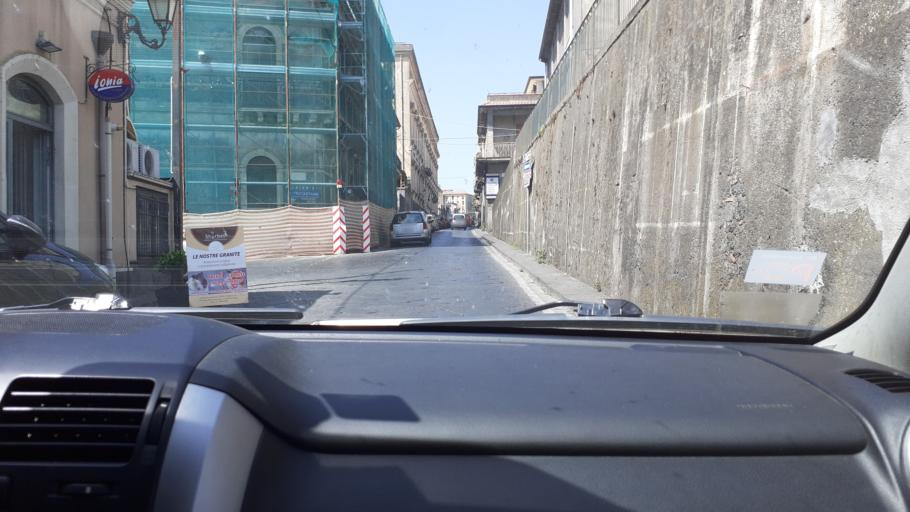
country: IT
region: Sicily
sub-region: Catania
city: Pedara
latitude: 37.6165
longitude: 15.0568
